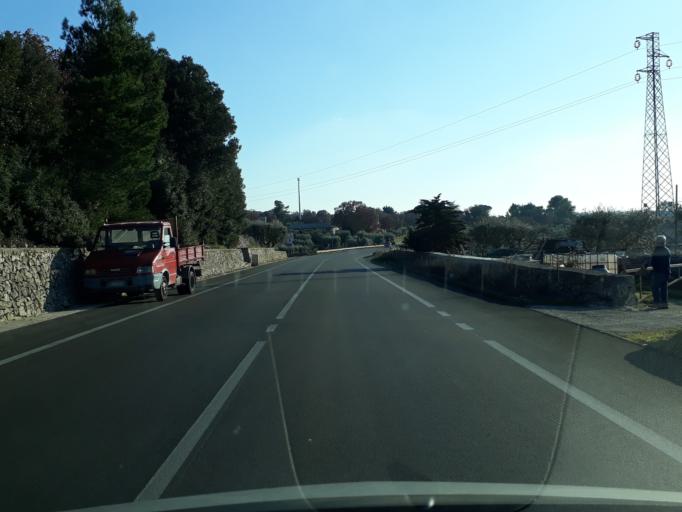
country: IT
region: Apulia
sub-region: Provincia di Bari
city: Locorotondo
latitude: 40.7816
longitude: 17.3389
